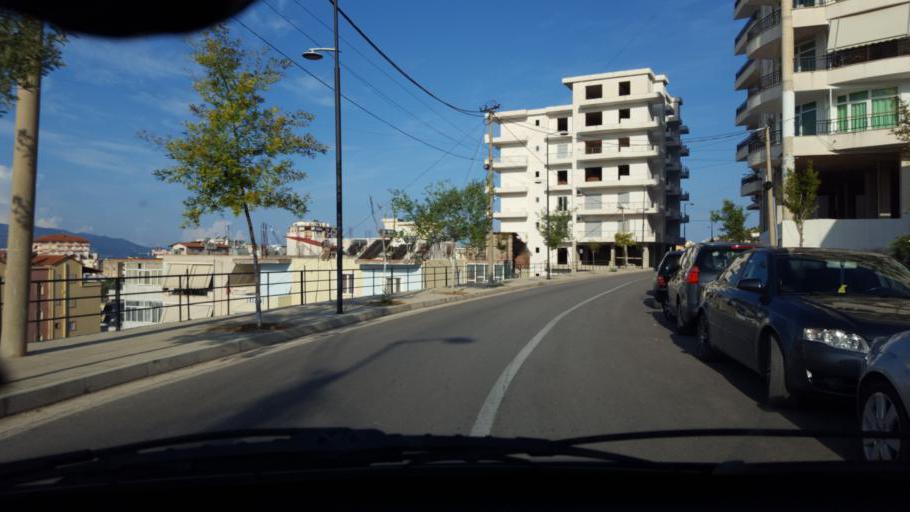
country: AL
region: Vlore
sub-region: Rrethi i Sarandes
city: Sarande
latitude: 39.8749
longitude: 19.9999
